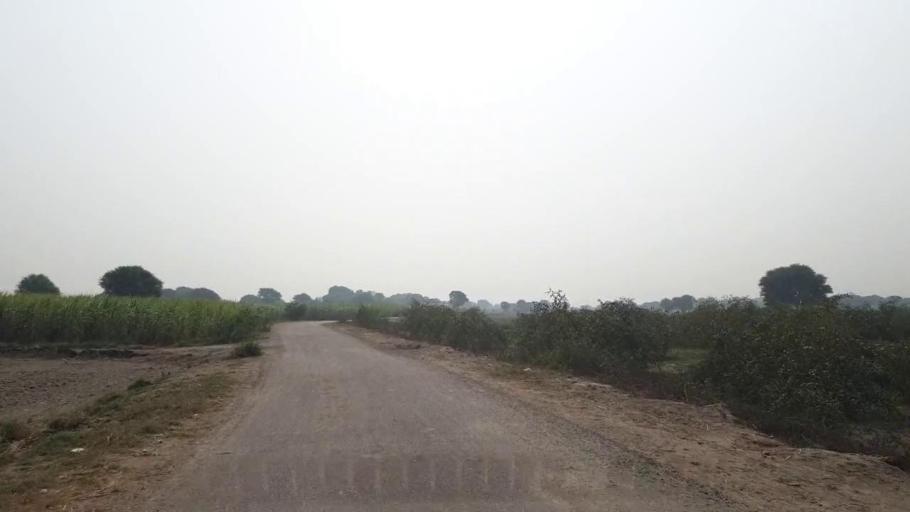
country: PK
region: Sindh
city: Tando Muhammad Khan
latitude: 25.1908
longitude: 68.6253
